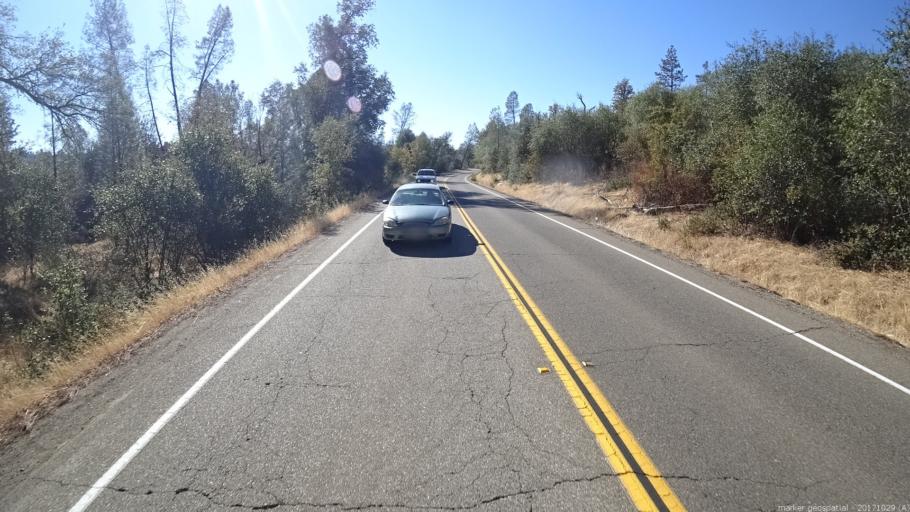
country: US
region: California
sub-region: Shasta County
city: Shasta
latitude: 40.4960
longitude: -122.4626
